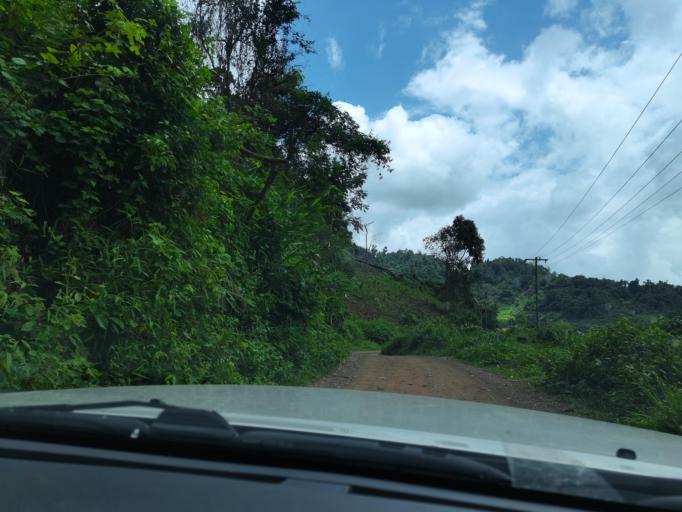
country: LA
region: Loungnamtha
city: Muang Long
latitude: 20.7466
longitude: 101.0188
